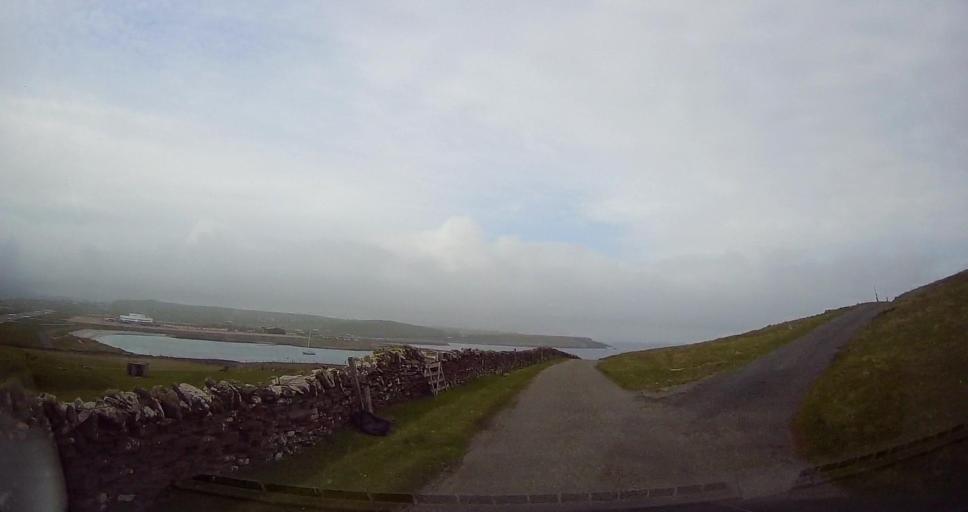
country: GB
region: Scotland
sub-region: Shetland Islands
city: Sandwick
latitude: 59.8684
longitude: -1.2790
